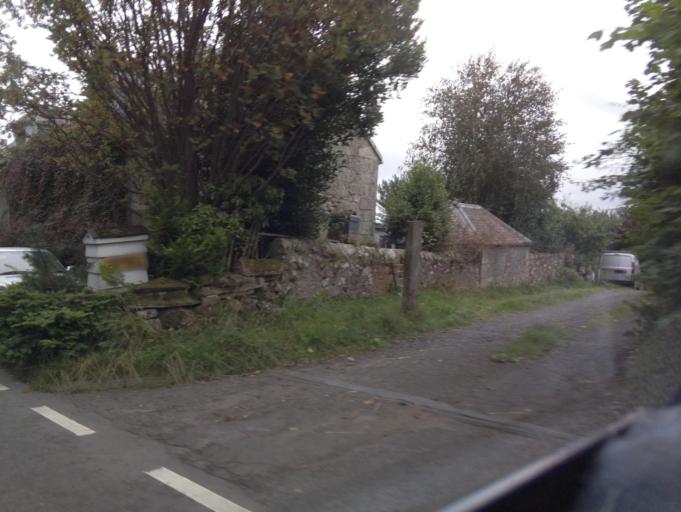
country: GB
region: Scotland
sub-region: Fife
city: Ballingry
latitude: 56.2077
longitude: -3.3258
